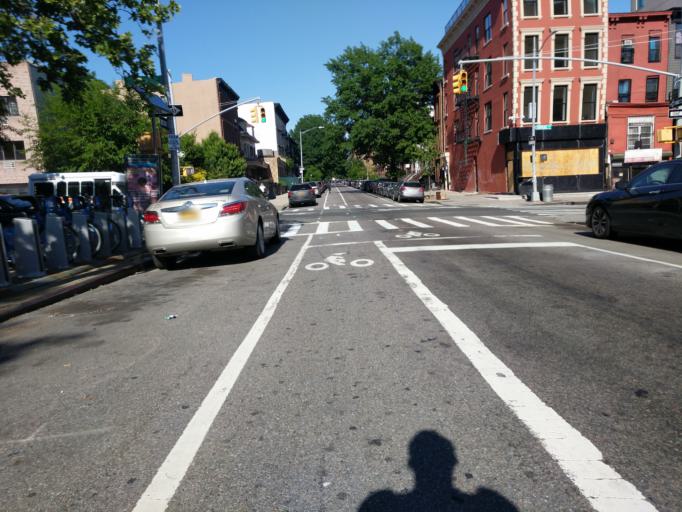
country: US
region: New York
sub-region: Kings County
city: Brooklyn
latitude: 40.6943
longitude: -73.9464
